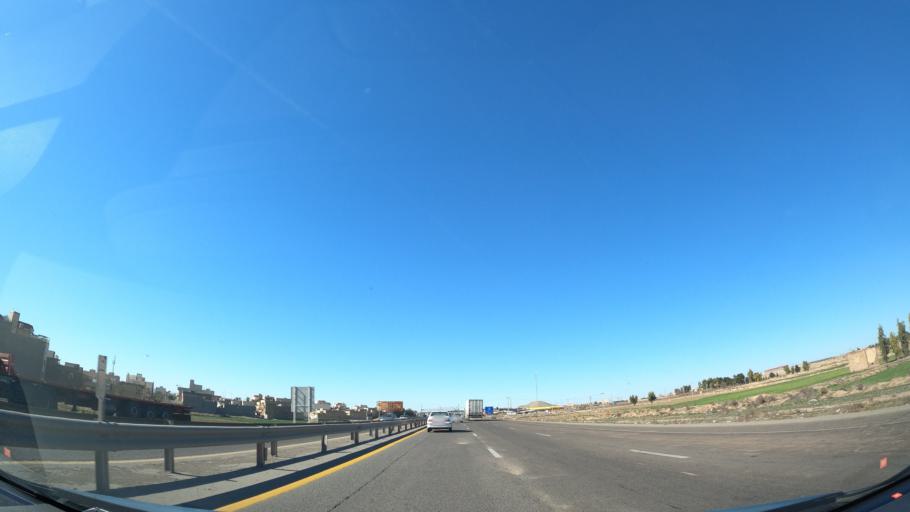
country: IR
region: Qom
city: Qom
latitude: 34.6681
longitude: 50.9174
